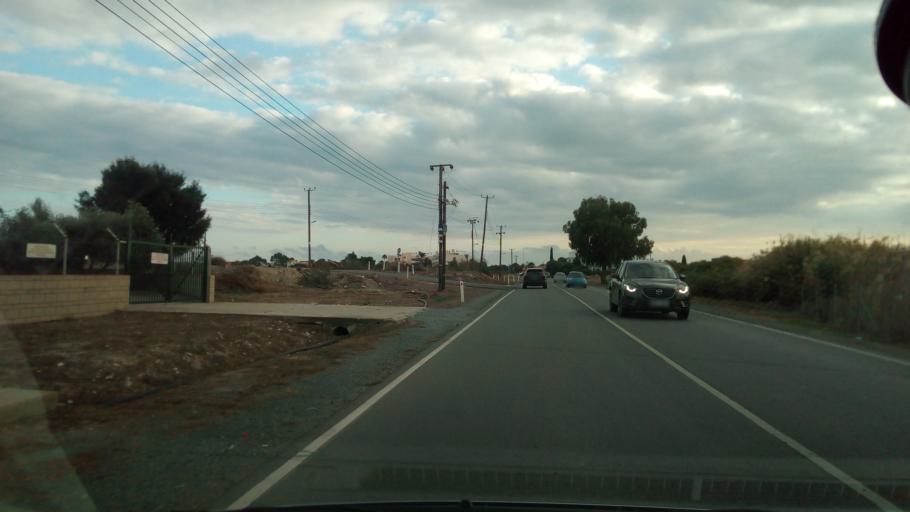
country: CY
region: Larnaka
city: Voroklini
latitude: 34.9667
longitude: 33.6575
